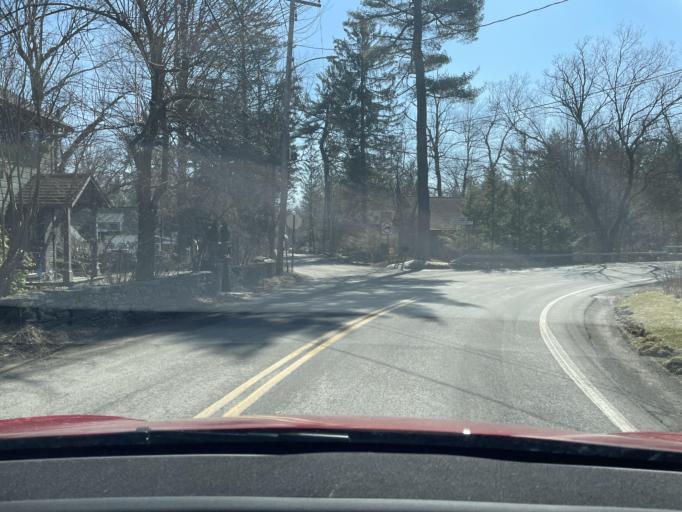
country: US
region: New York
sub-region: Ulster County
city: Woodstock
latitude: 42.0390
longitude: -74.1181
